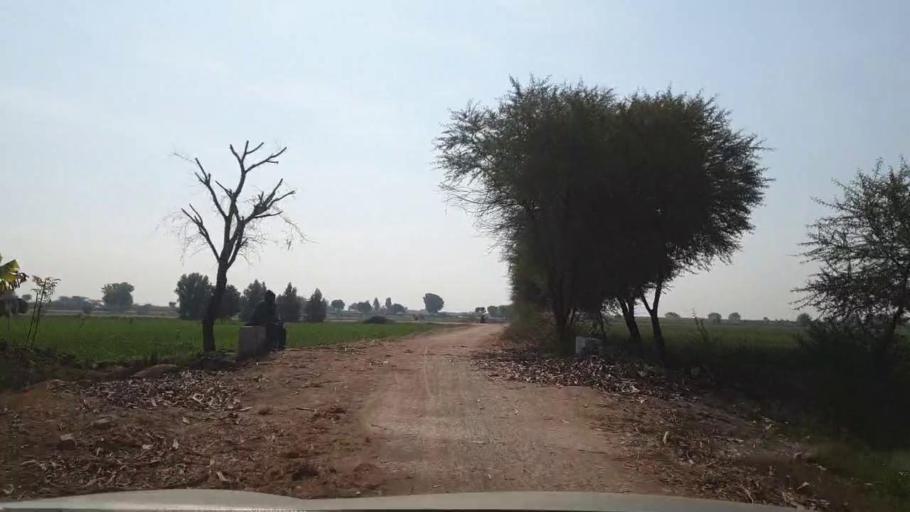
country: PK
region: Sindh
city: Tando Adam
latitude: 25.6488
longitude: 68.7403
